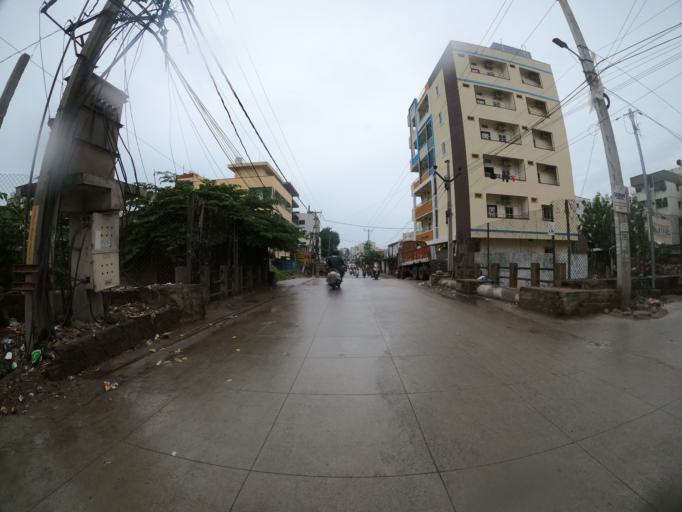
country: IN
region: Telangana
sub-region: Rangareddi
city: Kukatpalli
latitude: 17.4574
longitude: 78.4049
